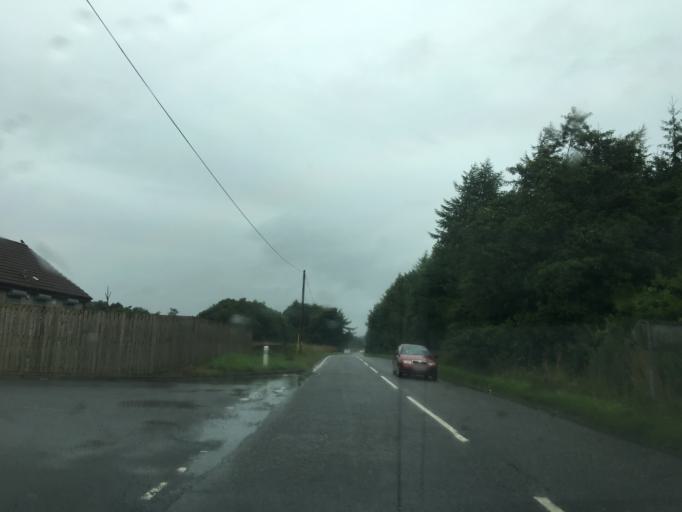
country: GB
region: Scotland
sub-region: Fife
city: Kelty
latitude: 56.1246
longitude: -3.4208
